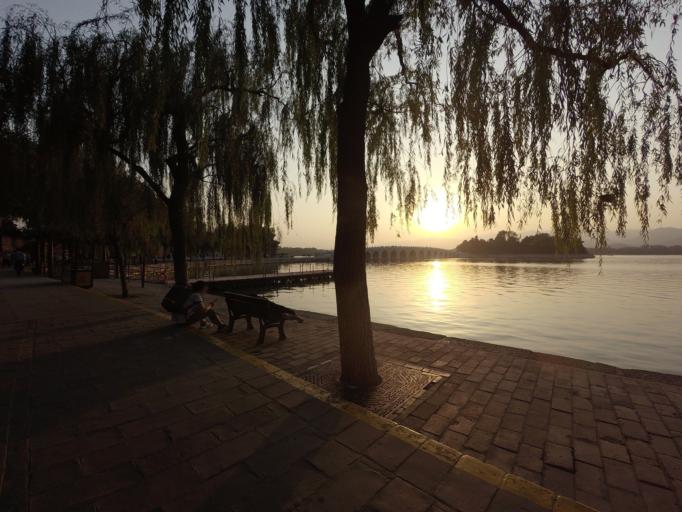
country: CN
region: Beijing
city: Haidian
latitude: 39.9899
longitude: 116.2737
